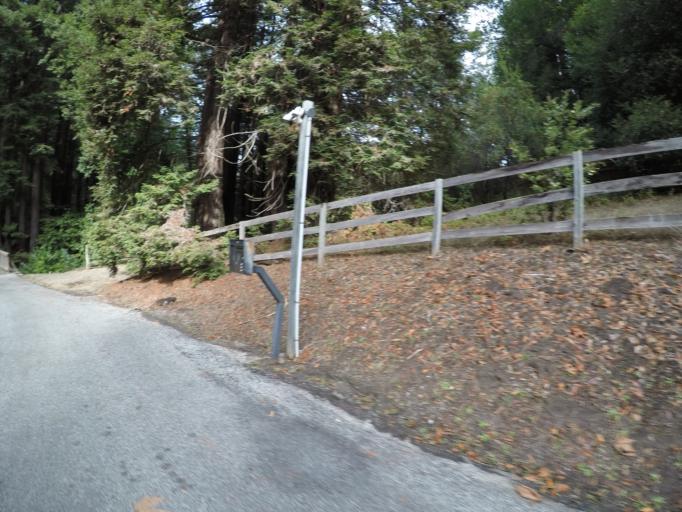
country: US
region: California
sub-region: Santa Cruz County
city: Scotts Valley
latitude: 37.0388
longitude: -121.9965
